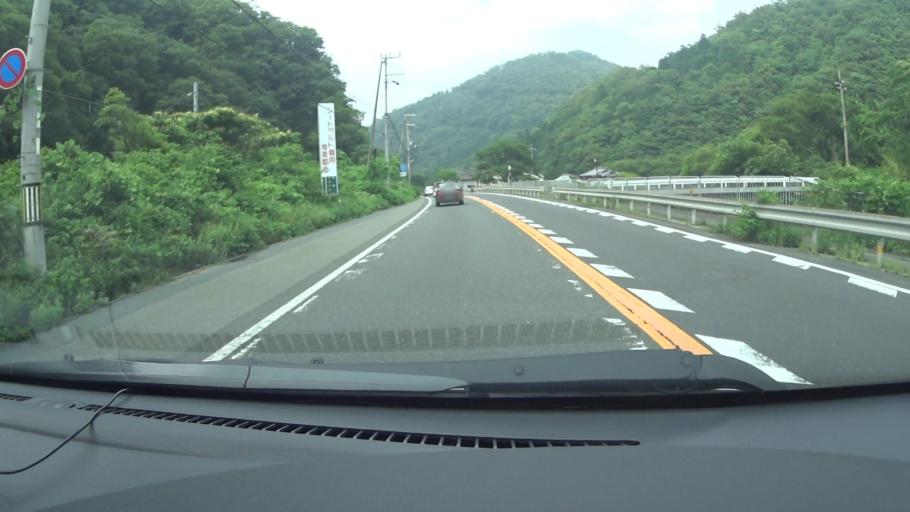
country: JP
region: Kyoto
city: Maizuru
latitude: 35.3899
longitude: 135.3169
